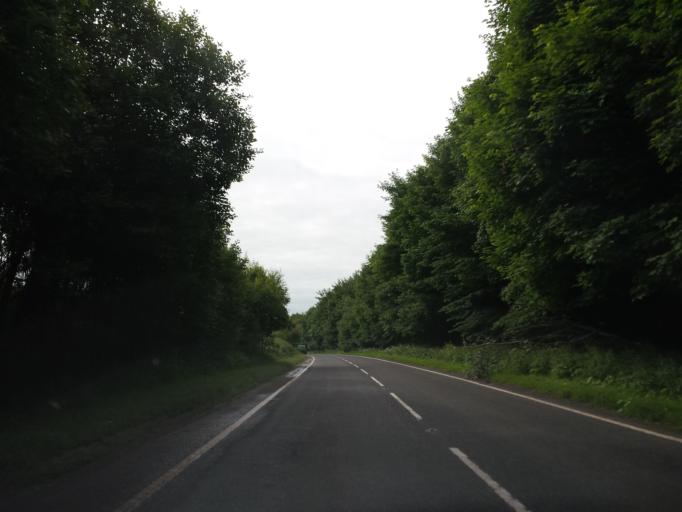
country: GB
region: Scotland
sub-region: Dumfries and Galloway
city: Moffat
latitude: 55.3213
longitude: -3.4678
